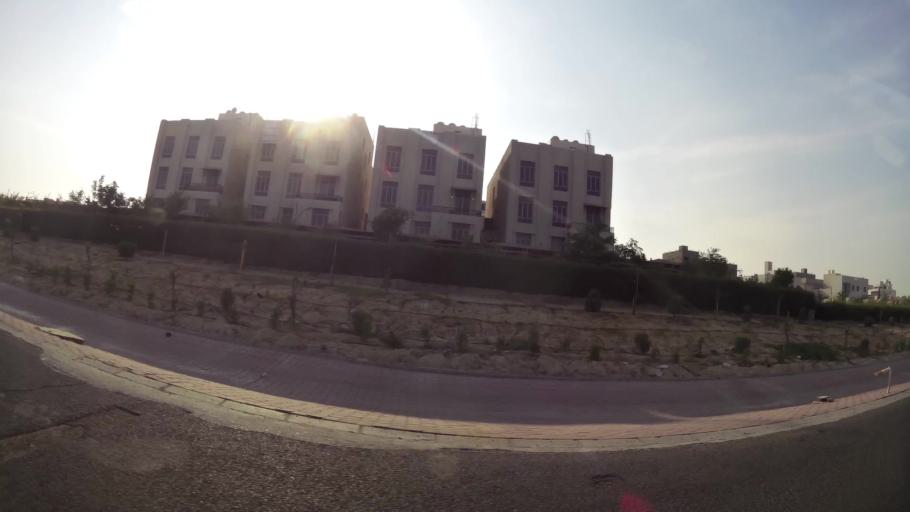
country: KW
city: Al Funaytis
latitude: 29.2038
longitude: 48.1058
